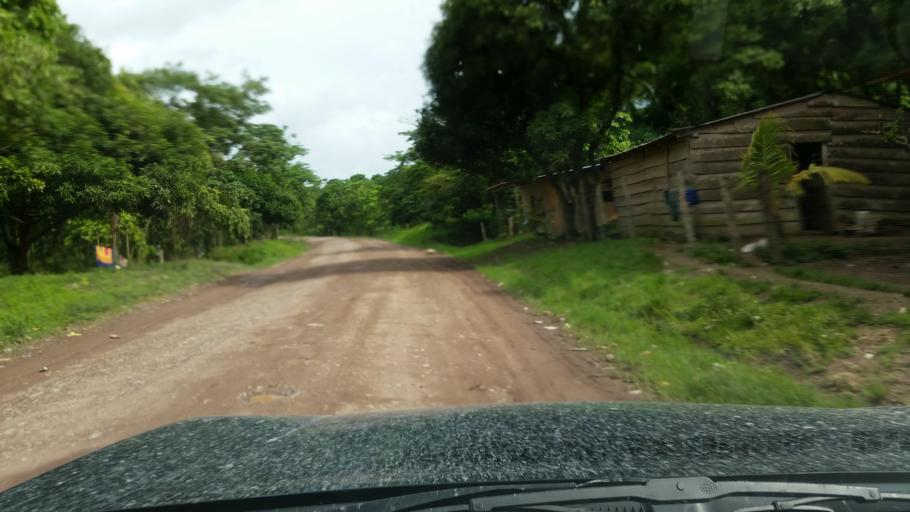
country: NI
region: Atlantico Norte (RAAN)
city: Siuna
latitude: 13.5057
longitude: -84.8443
